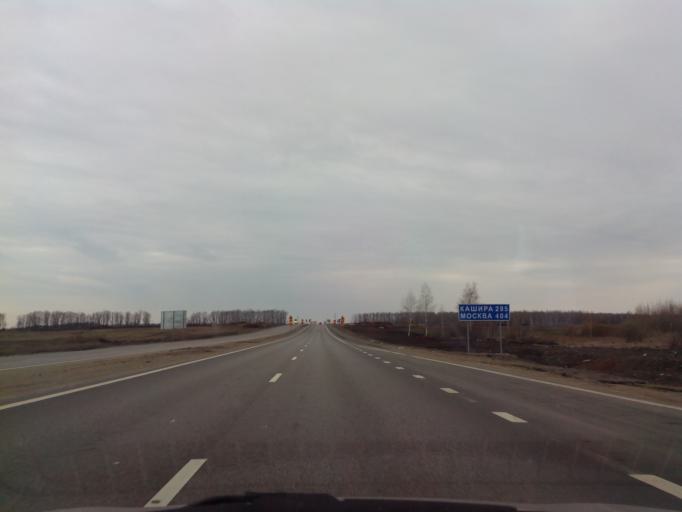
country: RU
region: Tambov
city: Zavoronezhskoye
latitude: 52.8887
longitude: 40.7065
